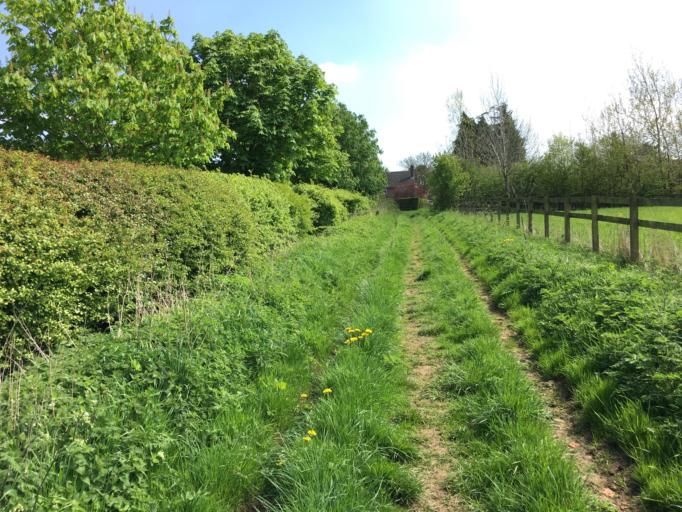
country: GB
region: England
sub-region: Leicestershire
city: Houghton on the Hill
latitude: 52.6037
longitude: -0.9786
